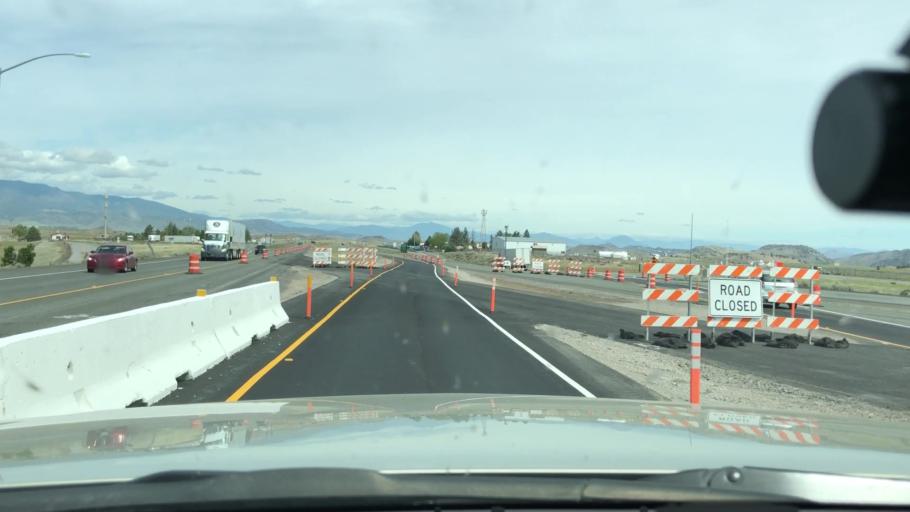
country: US
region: California
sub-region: Siskiyou County
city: Weed
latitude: 41.4729
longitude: -122.4529
